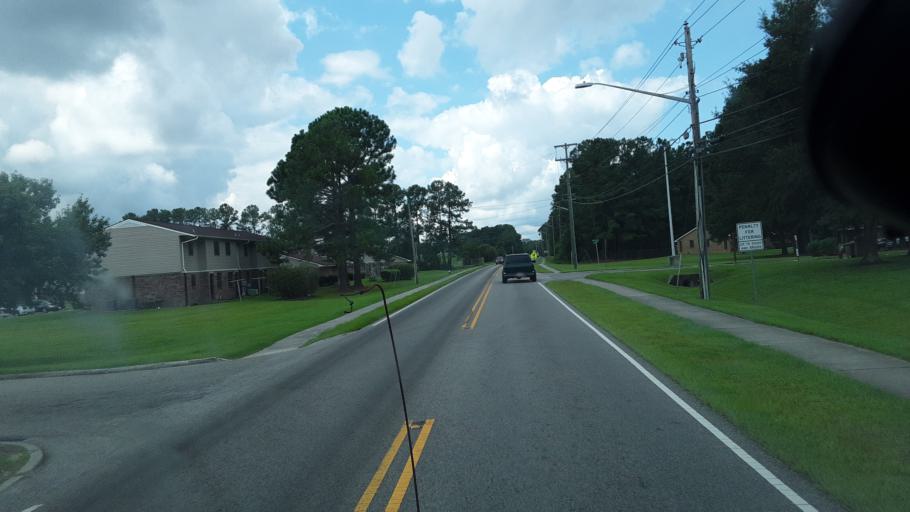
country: US
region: South Carolina
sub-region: Georgetown County
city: Georgetown
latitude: 33.3875
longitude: -79.2949
